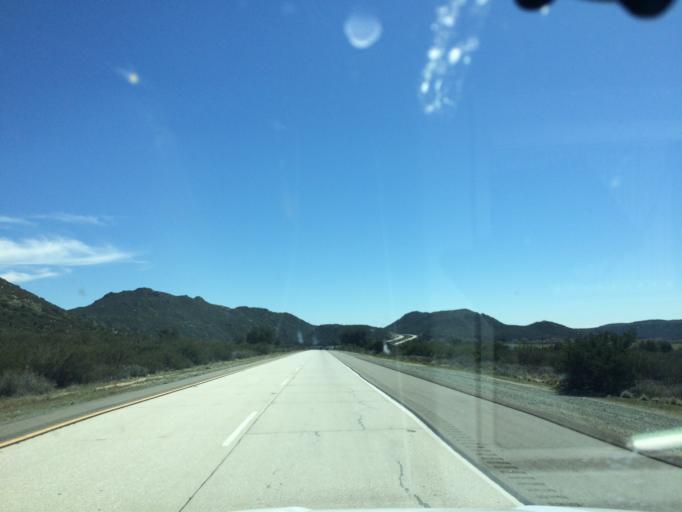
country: US
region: California
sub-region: San Diego County
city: Pine Valley
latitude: 32.7534
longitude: -116.4835
